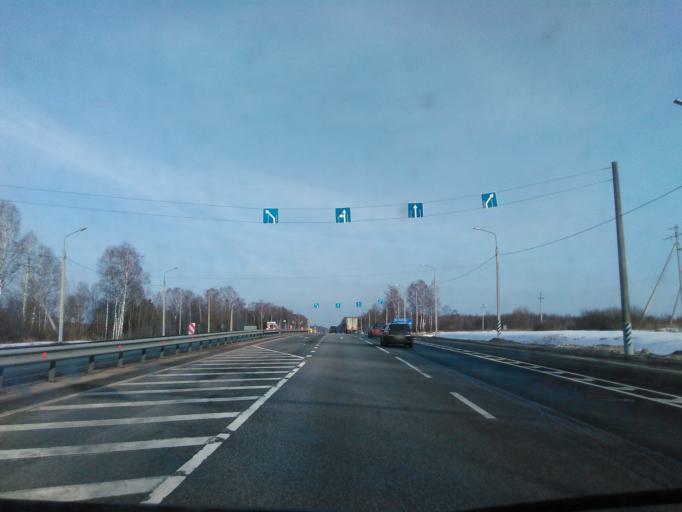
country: RU
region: Smolensk
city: Kholm-Zhirkovskiy
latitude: 55.1887
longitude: 33.7530
